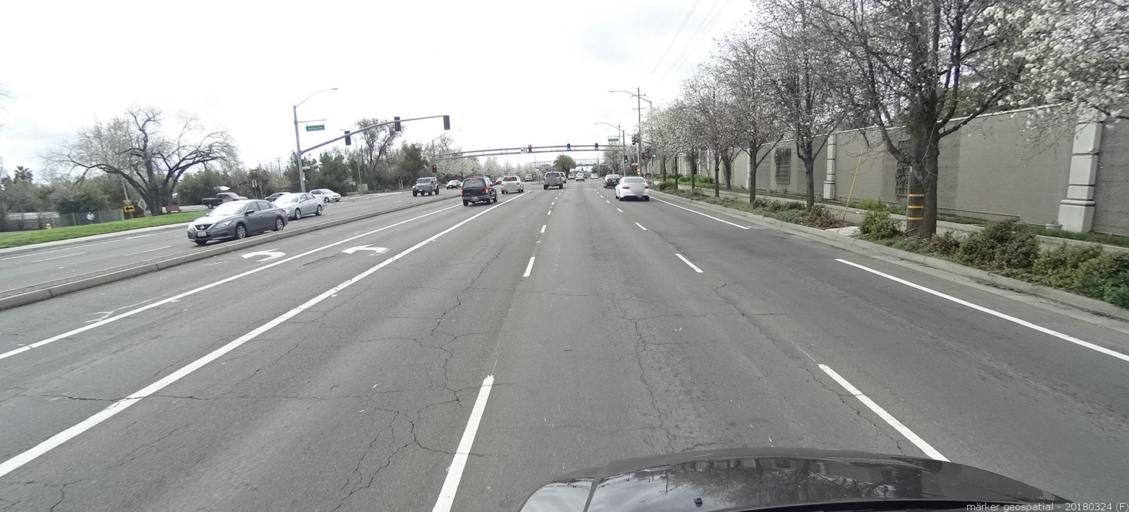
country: US
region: California
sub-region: Sacramento County
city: North Highlands
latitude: 38.6638
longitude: -121.3829
